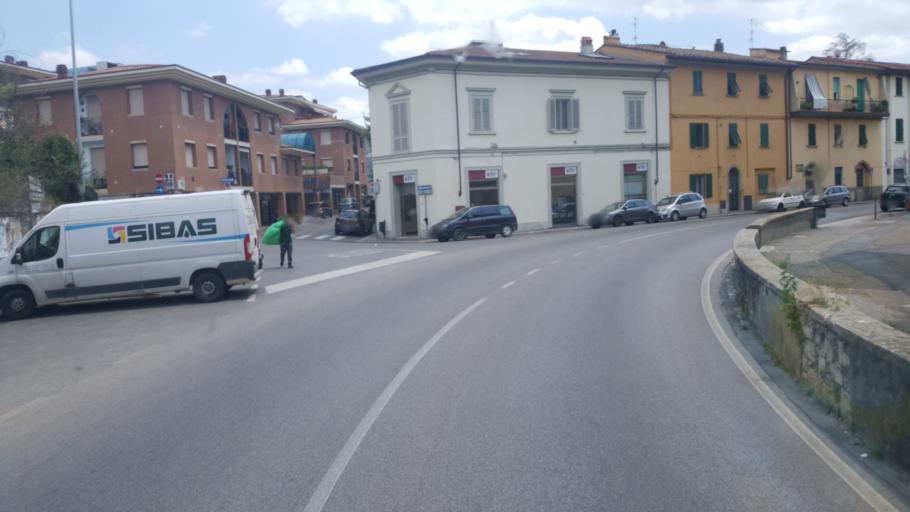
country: IT
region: Tuscany
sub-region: Province of Florence
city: Sieci
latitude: 43.7913
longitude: 11.3922
